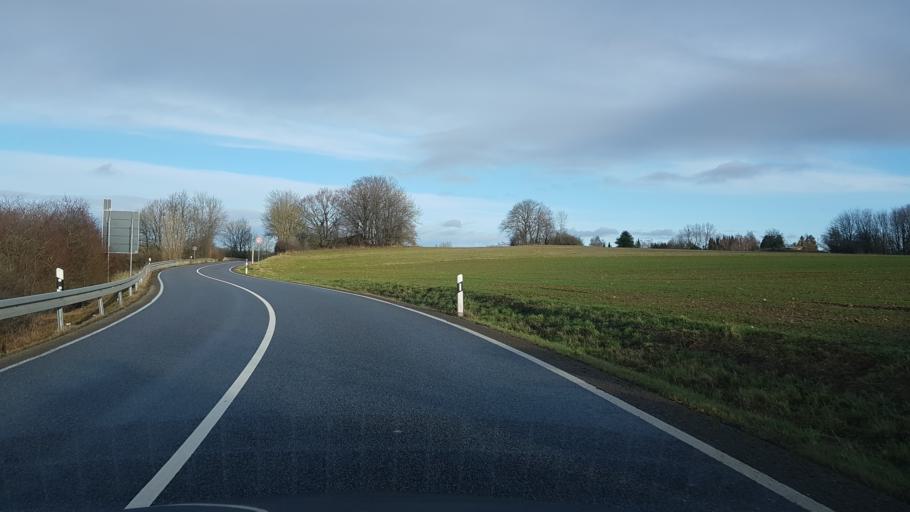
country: DE
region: Saarland
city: Sankt Ingbert
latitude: 49.2355
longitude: 7.1265
